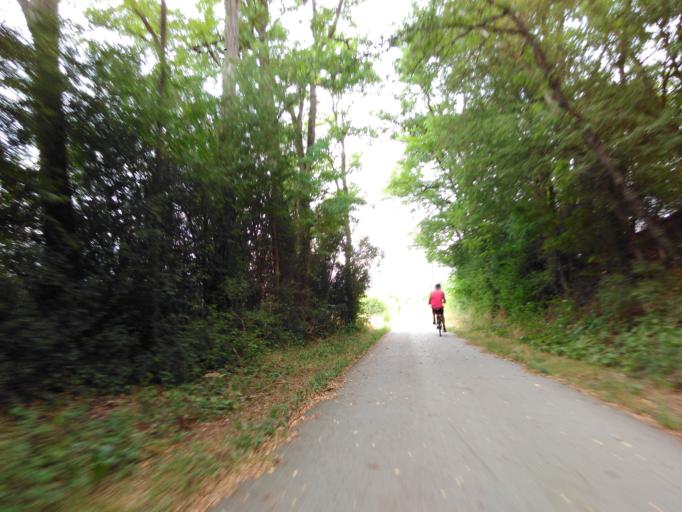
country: LU
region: Grevenmacher
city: Gonderange
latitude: 49.6862
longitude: 6.2497
